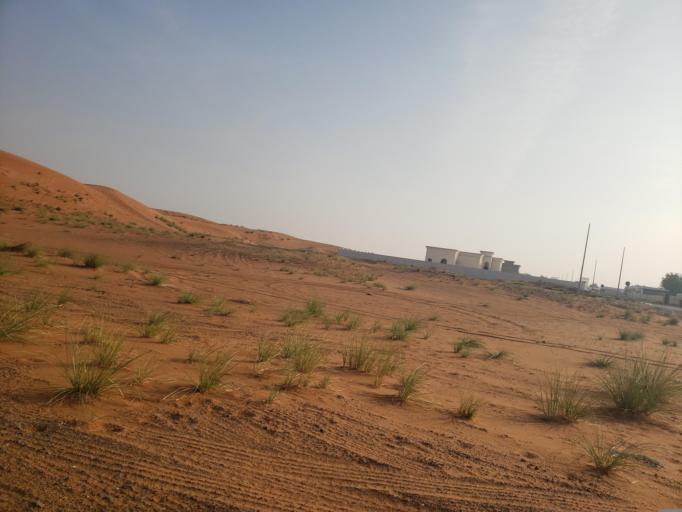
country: AE
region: Ash Shariqah
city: Adh Dhayd
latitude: 25.1360
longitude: 55.8426
